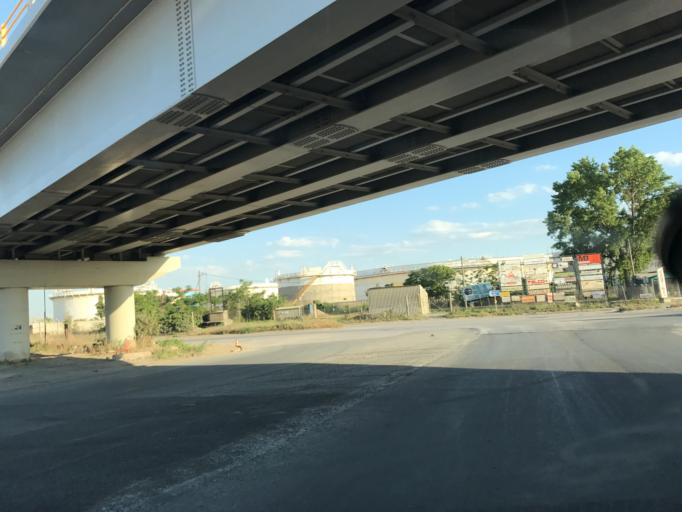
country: GR
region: Central Macedonia
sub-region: Nomos Thessalonikis
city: Menemeni
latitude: 40.6509
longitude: 22.8816
